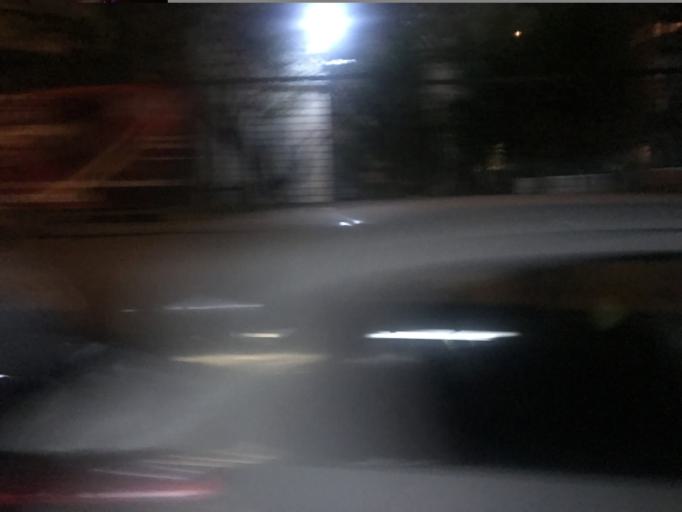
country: TR
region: Istanbul
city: Bahcelievler
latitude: 40.9816
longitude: 28.8678
